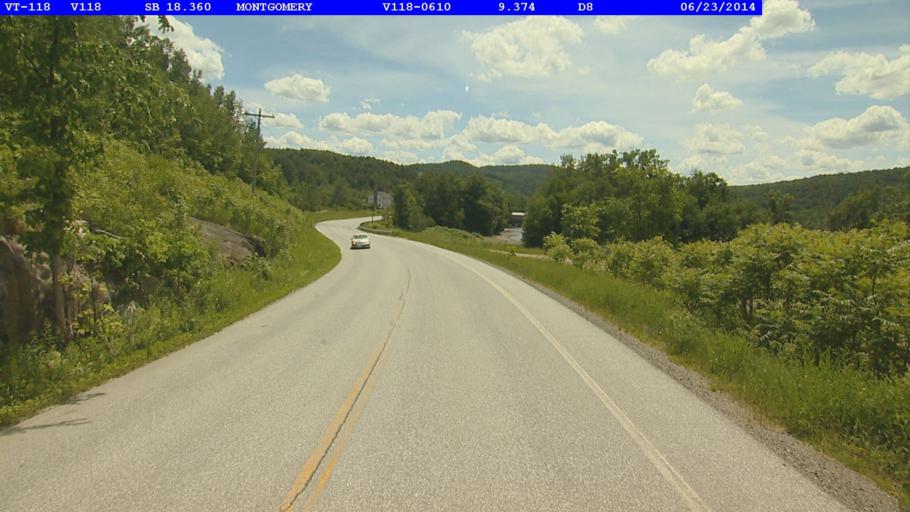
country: US
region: Vermont
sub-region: Franklin County
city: Richford
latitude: 44.9106
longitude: -72.6582
